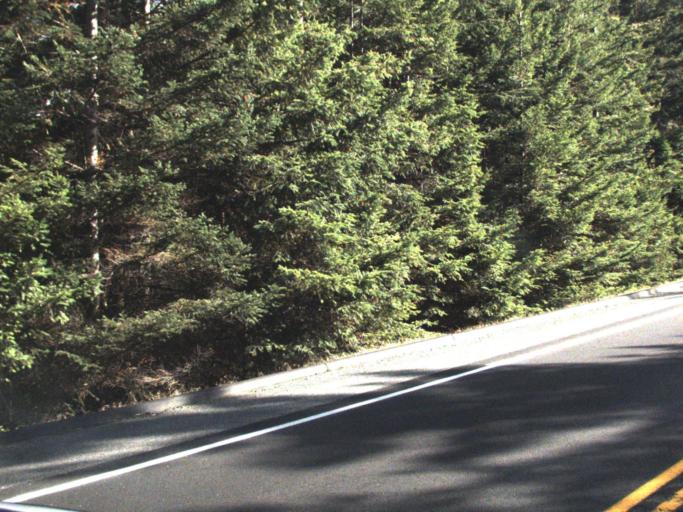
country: US
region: Washington
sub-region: Island County
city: Coupeville
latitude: 48.2257
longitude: -122.7383
